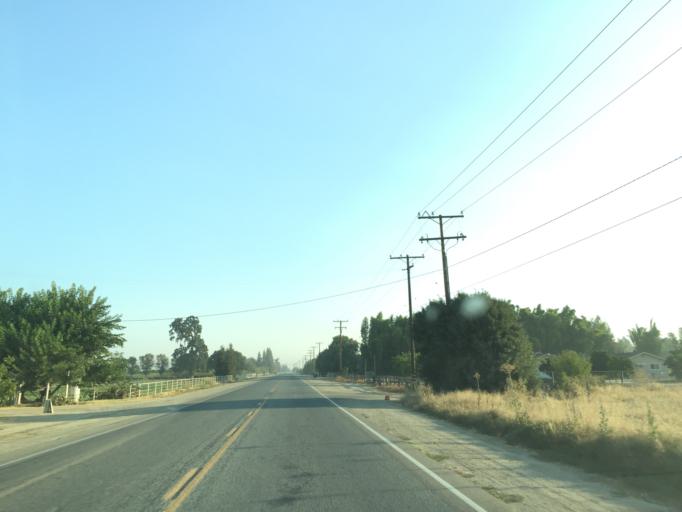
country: US
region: California
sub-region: Tulare County
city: Visalia
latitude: 36.3778
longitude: -119.2788
